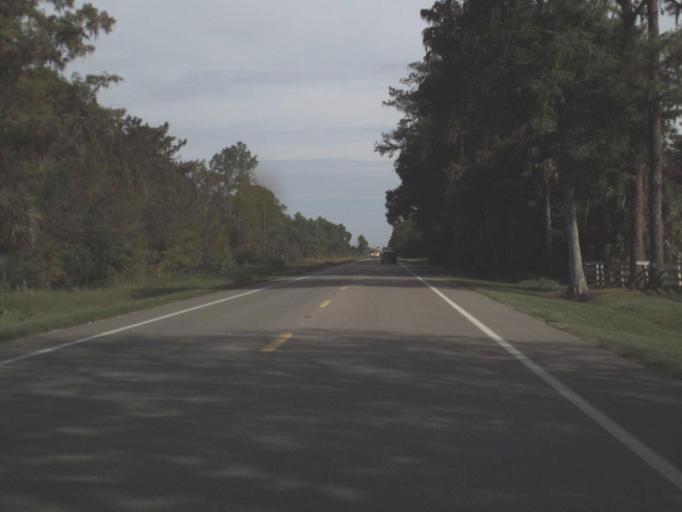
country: US
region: Florida
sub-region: Charlotte County
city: Cleveland
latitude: 26.9695
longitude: -81.7606
